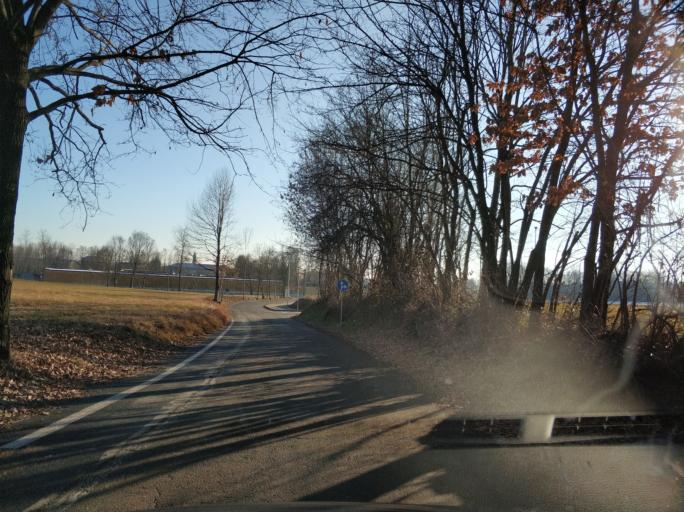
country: IT
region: Piedmont
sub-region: Provincia di Torino
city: San Francesco al Campo
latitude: 45.2334
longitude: 7.6552
